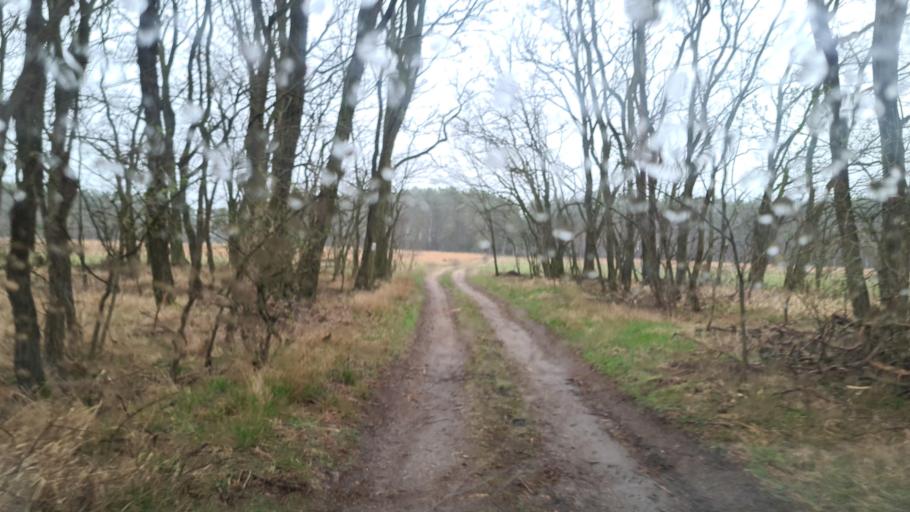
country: DE
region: Brandenburg
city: Bruck
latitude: 52.1615
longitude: 12.7210
